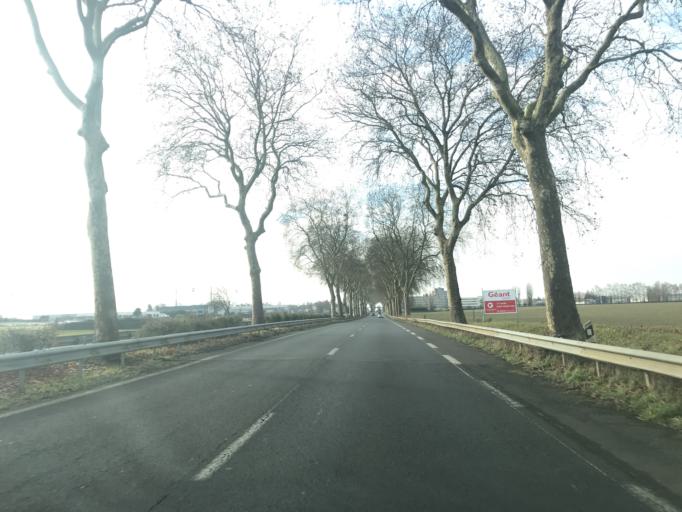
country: FR
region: Poitou-Charentes
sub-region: Departement des Deux-Sevres
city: Chauray
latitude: 46.3461
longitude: -0.3642
